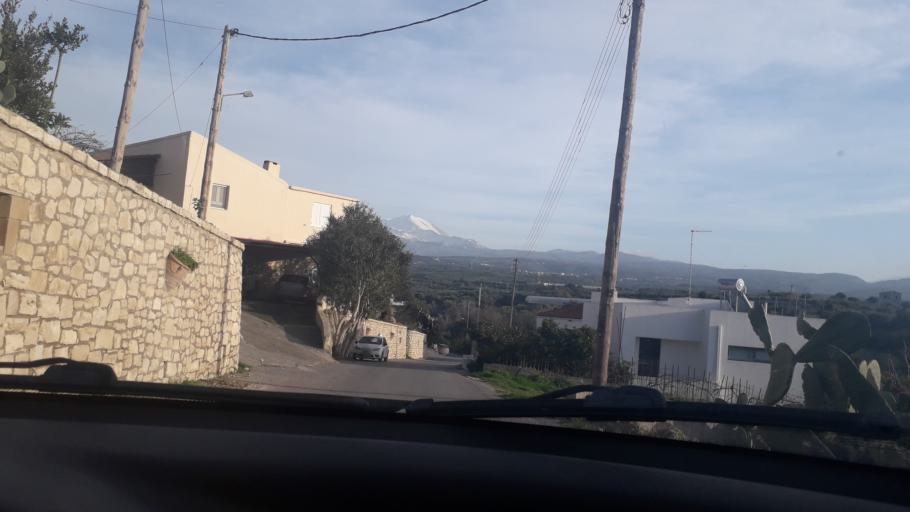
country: GR
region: Crete
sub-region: Nomos Rethymnis
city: Panormos
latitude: 35.3830
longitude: 24.6195
